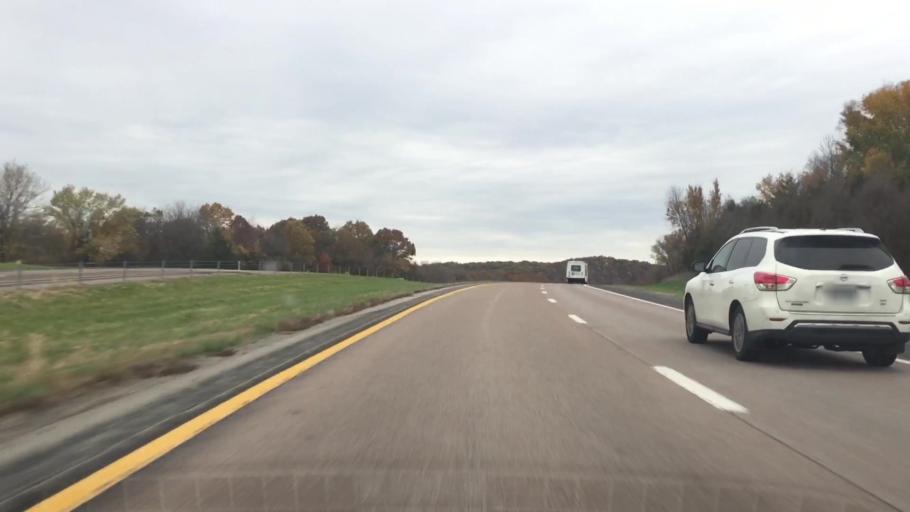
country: US
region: Missouri
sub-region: Cole County
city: Jefferson City
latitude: 38.6525
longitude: -92.2101
